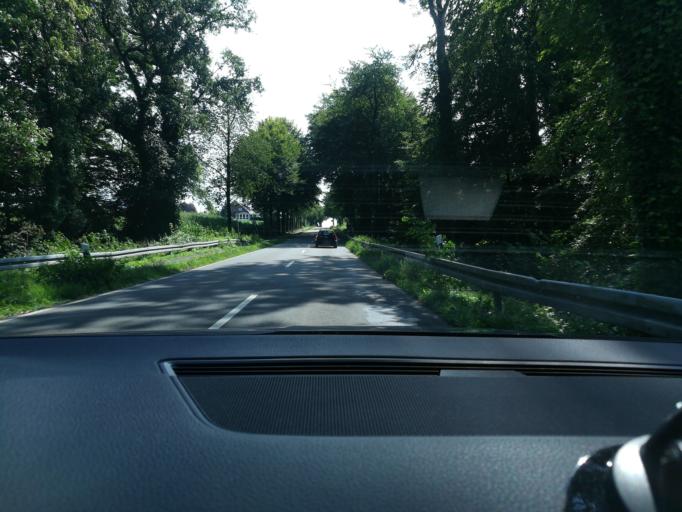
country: DE
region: North Rhine-Westphalia
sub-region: Regierungsbezirk Detmold
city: Huellhorst
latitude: 52.2790
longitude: 8.6998
